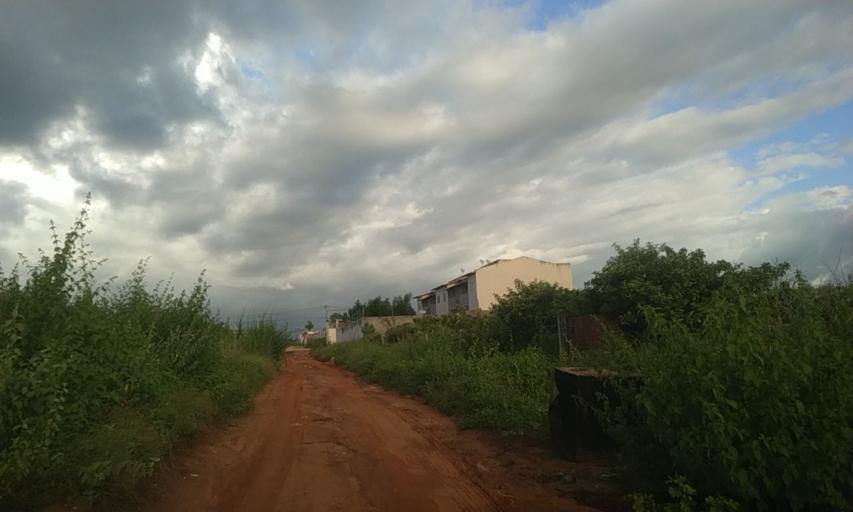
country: BR
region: Rio Grande do Norte
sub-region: Mossoro
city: Mossoro
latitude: -5.2211
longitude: -37.3435
